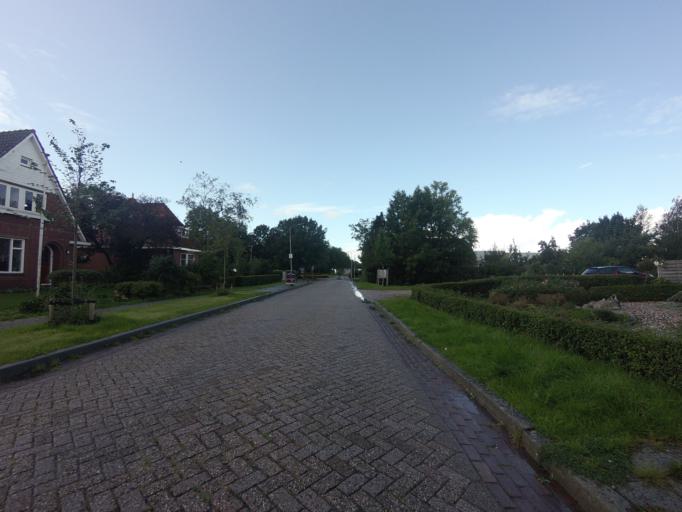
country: NL
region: Friesland
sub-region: Gemeente Boarnsterhim
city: Warten
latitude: 53.1494
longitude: 5.8935
